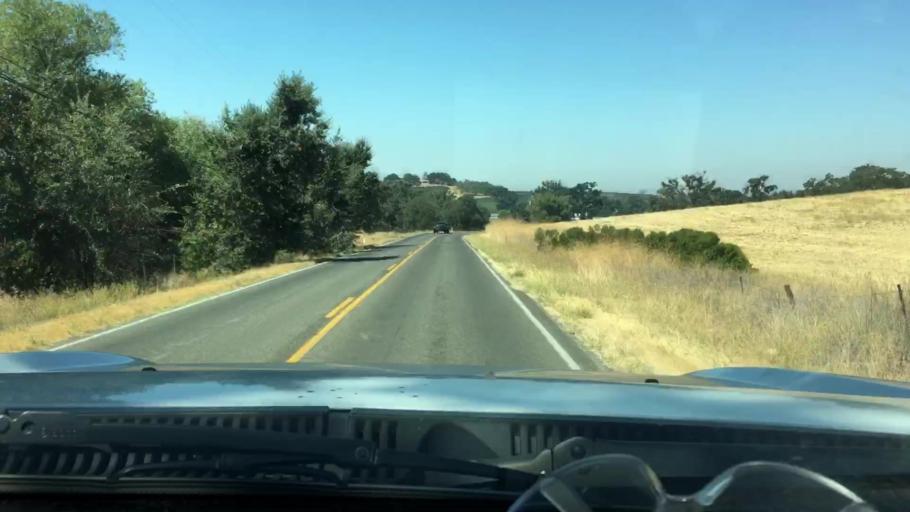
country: US
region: California
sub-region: San Luis Obispo County
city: Paso Robles
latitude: 35.5844
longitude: -120.6196
